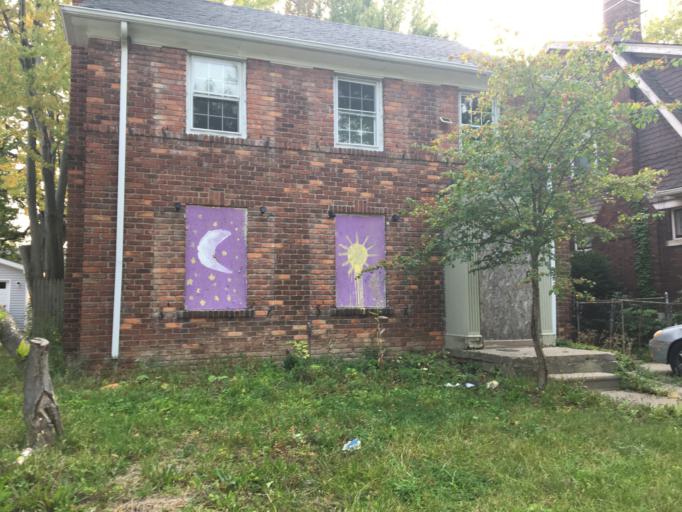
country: US
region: Michigan
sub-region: Wayne County
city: Grosse Pointe Park
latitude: 42.3947
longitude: -82.9398
